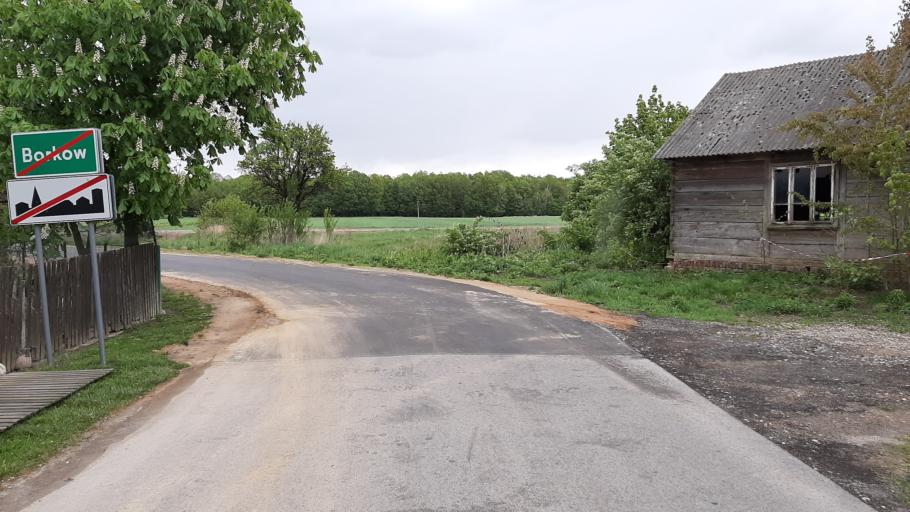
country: PL
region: Lublin Voivodeship
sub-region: Powiat lubelski
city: Garbow
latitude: 51.3799
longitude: 22.4010
